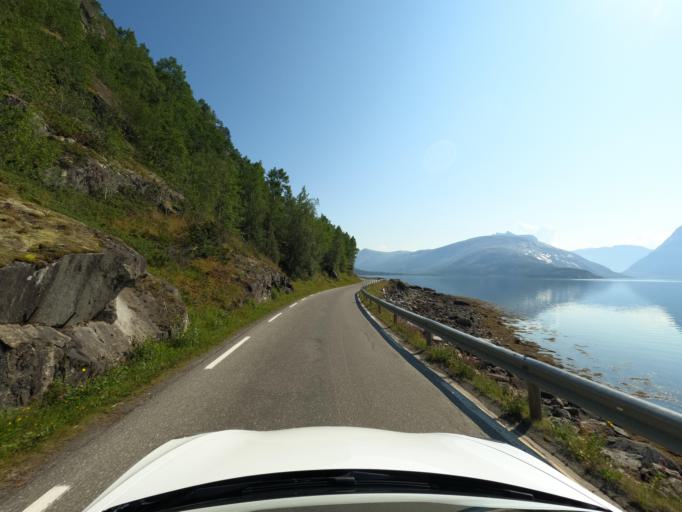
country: NO
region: Nordland
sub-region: Narvik
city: Narvik
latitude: 68.2874
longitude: 17.3683
